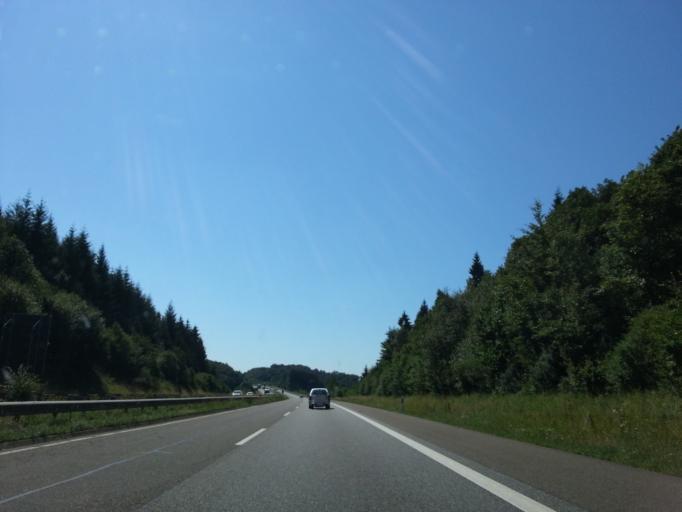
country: DE
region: Rheinland-Pfalz
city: Orlenbach
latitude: 50.1671
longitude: 6.3913
